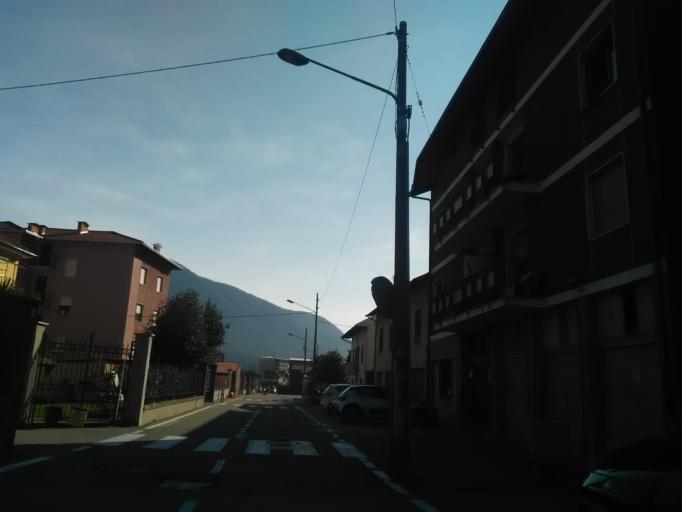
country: IT
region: Piedmont
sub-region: Provincia di Vercelli
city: Borgosesia
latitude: 45.7089
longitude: 8.2794
